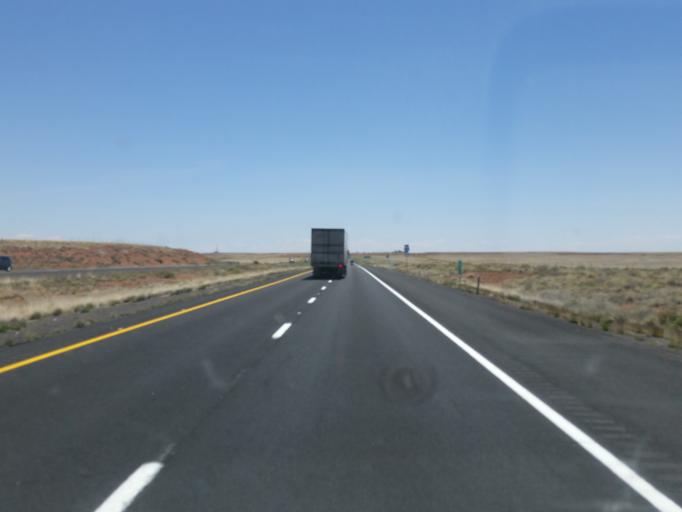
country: US
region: Arizona
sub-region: Coconino County
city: LeChee
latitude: 35.1160
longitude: -111.0821
